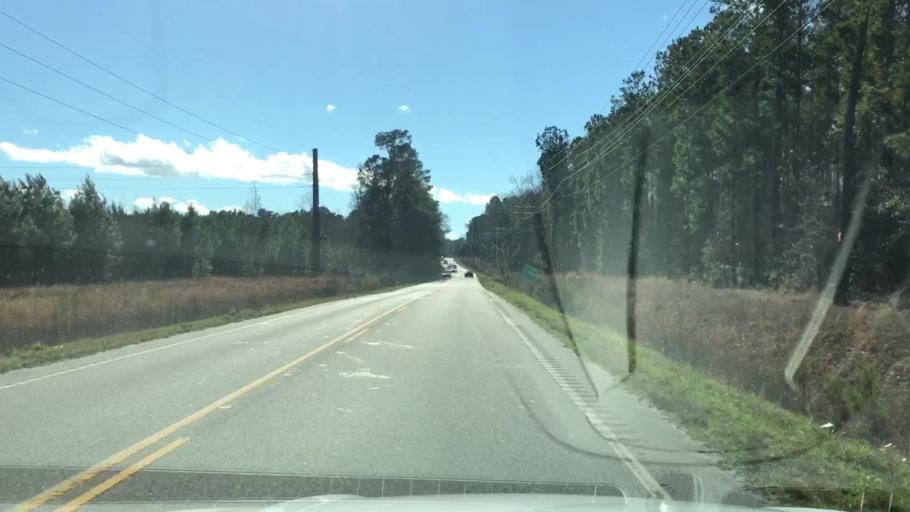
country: US
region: South Carolina
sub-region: Dorchester County
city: Summerville
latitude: 33.0745
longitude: -80.2174
